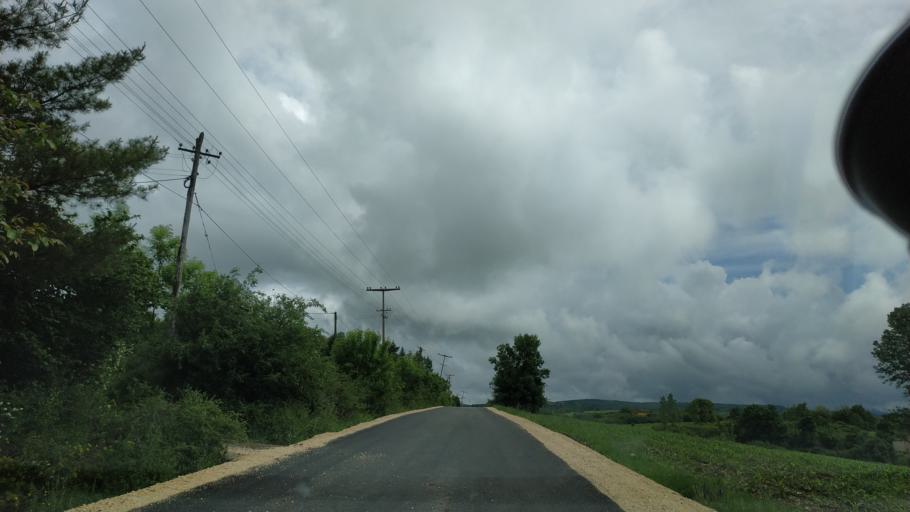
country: RS
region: Central Serbia
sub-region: Zajecarski Okrug
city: Soko Banja
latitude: 43.6465
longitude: 21.8986
